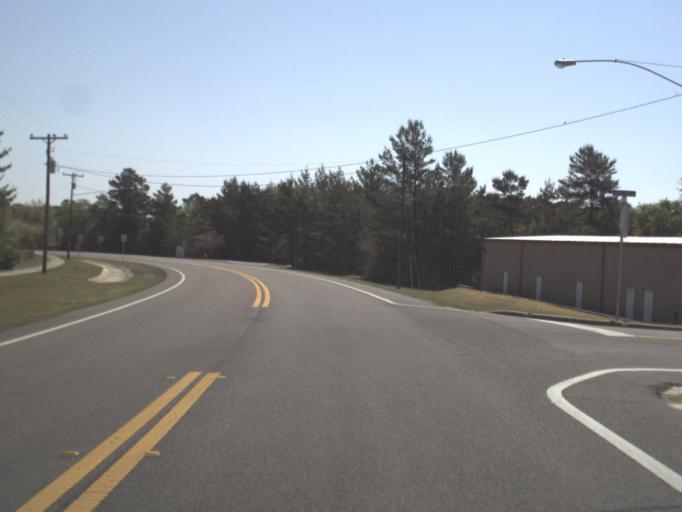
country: US
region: Florida
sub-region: Okaloosa County
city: Valparaiso
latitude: 30.5096
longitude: -86.4985
